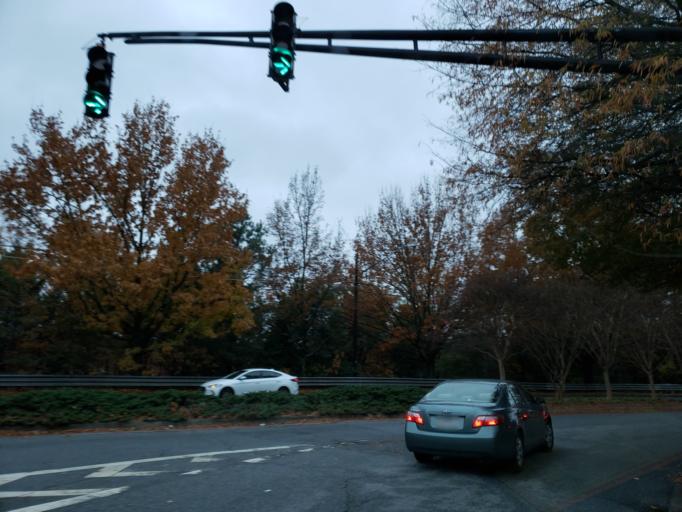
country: US
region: Georgia
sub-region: DeKalb County
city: Druid Hills
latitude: 33.8209
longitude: -84.3690
